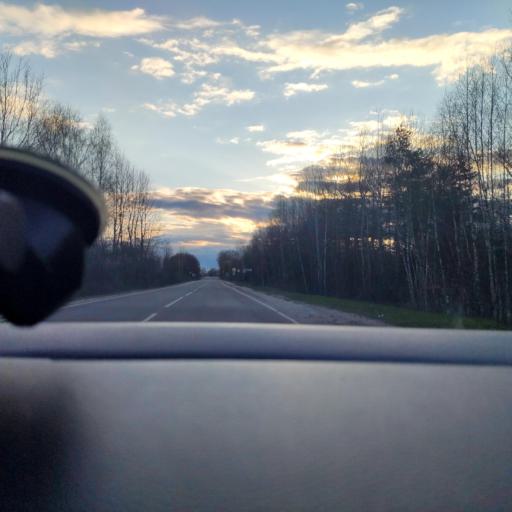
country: RU
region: Moskovskaya
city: Krasnyy Tkach
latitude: 55.4286
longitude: 39.2104
